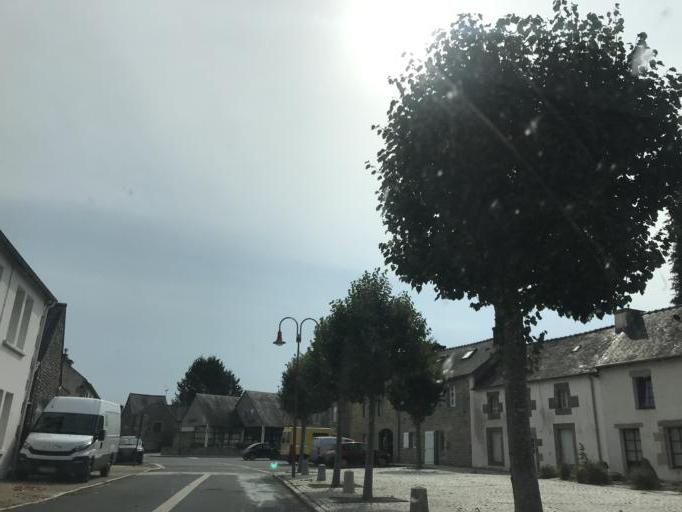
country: FR
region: Brittany
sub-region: Departement du Finistere
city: Plouneour-Menez
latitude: 48.3582
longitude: -3.8513
